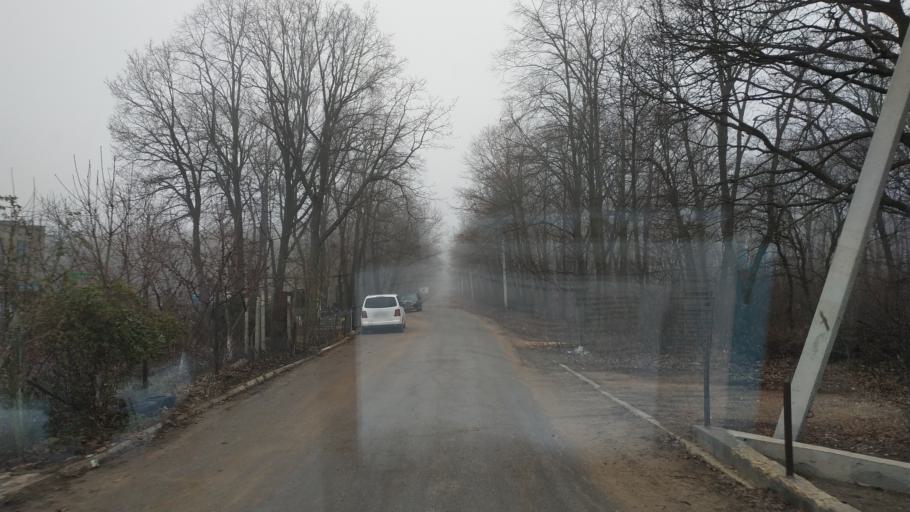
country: MD
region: Laloveni
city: Ialoveni
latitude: 46.9530
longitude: 28.6981
